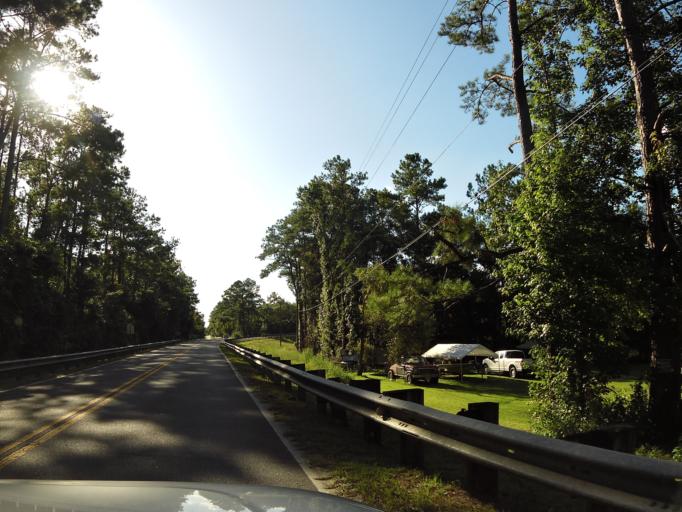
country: US
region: Florida
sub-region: Wakulla County
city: Crawfordville
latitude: 30.0624
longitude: -84.4982
